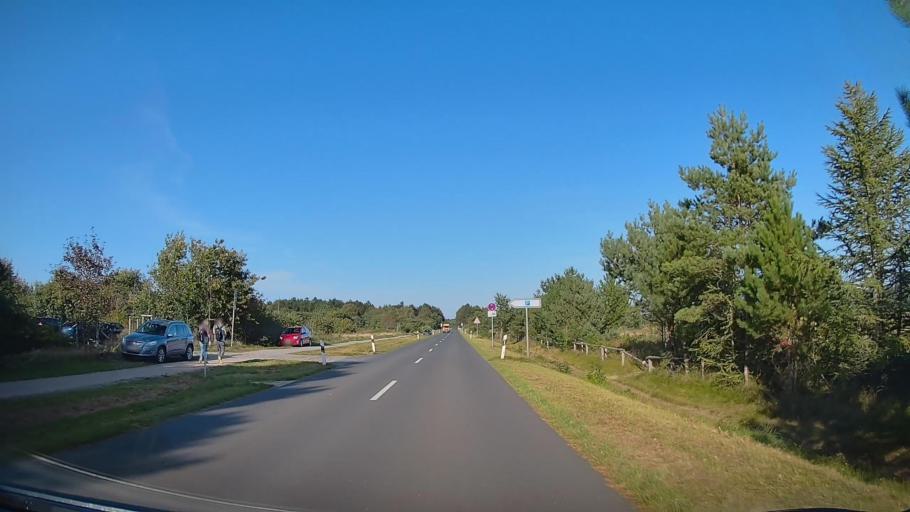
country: DE
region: Lower Saxony
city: Nordholz
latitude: 53.8398
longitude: 8.6206
